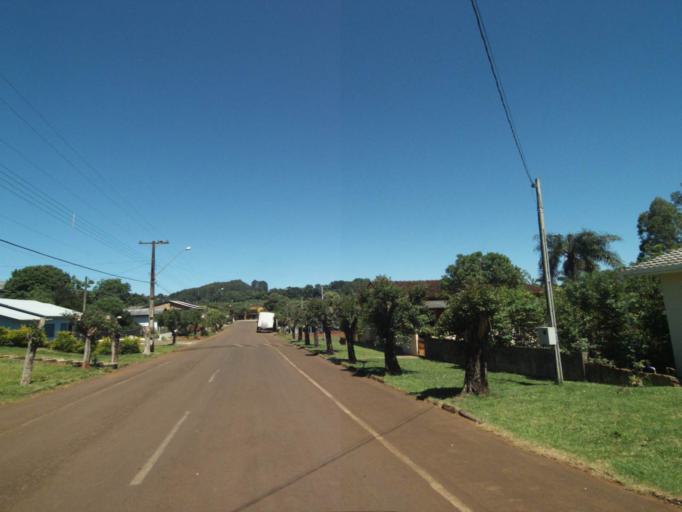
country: BR
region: Parana
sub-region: Pato Branco
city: Pato Branco
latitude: -26.2646
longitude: -52.7778
